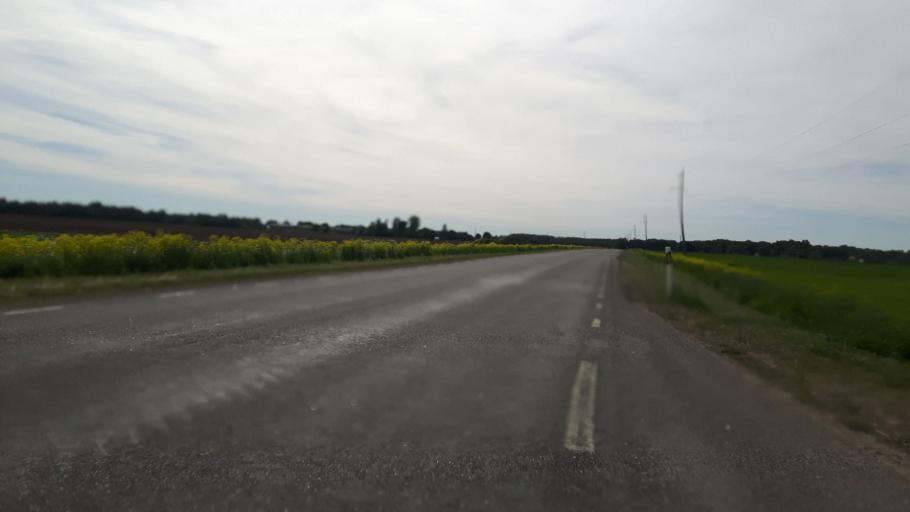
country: EE
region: Harju
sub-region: Maardu linn
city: Maardu
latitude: 59.4254
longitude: 25.0417
